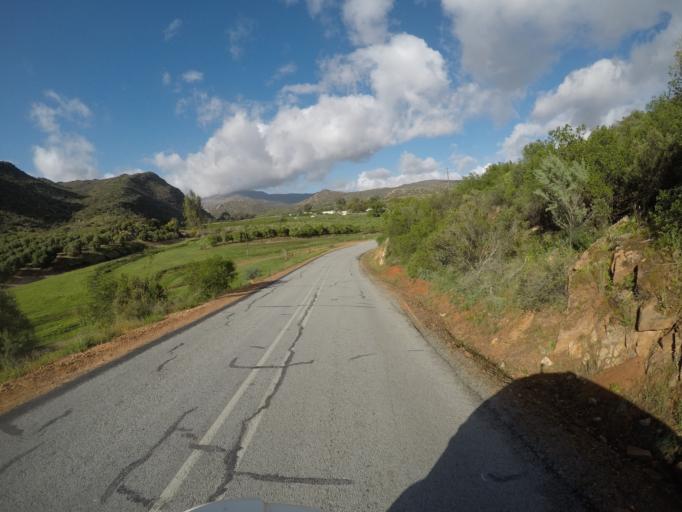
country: ZA
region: Western Cape
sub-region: West Coast District Municipality
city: Clanwilliam
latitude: -32.4370
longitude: 18.9456
